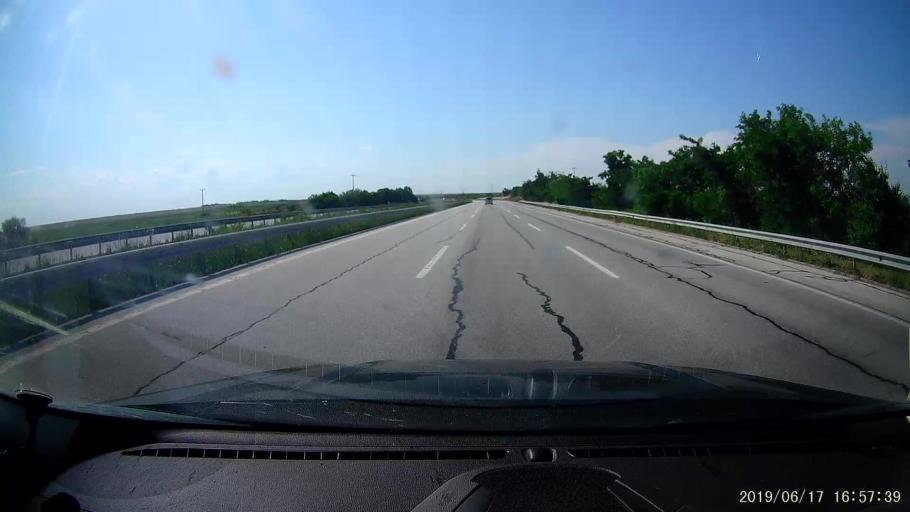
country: TR
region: Edirne
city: Haskoy
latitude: 41.6042
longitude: 26.9095
